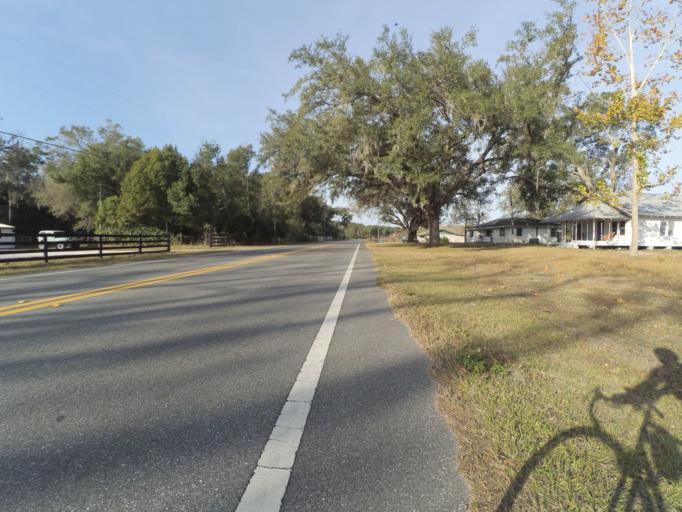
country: US
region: Florida
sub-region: Lake County
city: Umatilla
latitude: 28.9640
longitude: -81.6426
